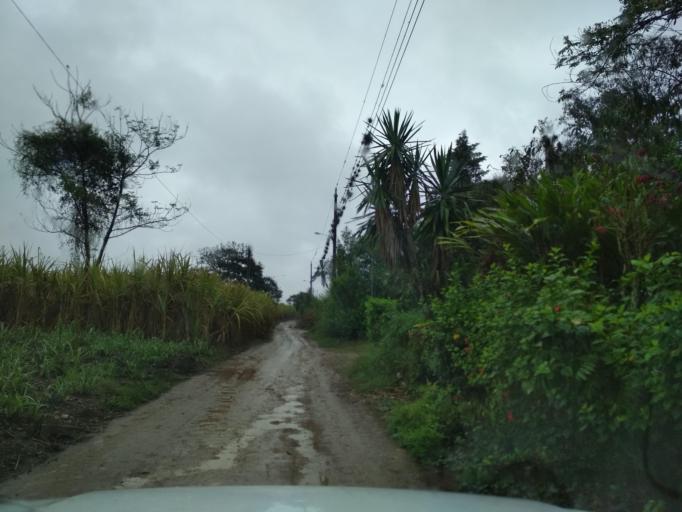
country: MX
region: Veracruz
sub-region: Amatlan de los Reyes
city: Centro de Readaptacion Social
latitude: 18.8322
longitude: -96.9313
